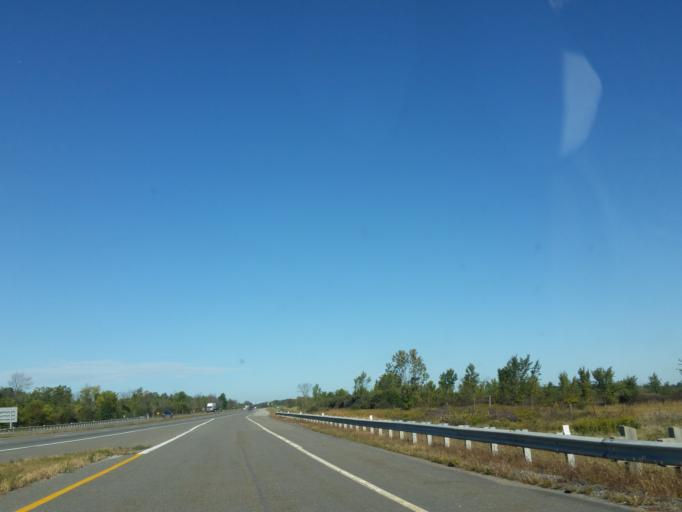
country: US
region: New York
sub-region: Niagara County
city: Niagara Falls
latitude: 42.9922
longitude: -79.0596
